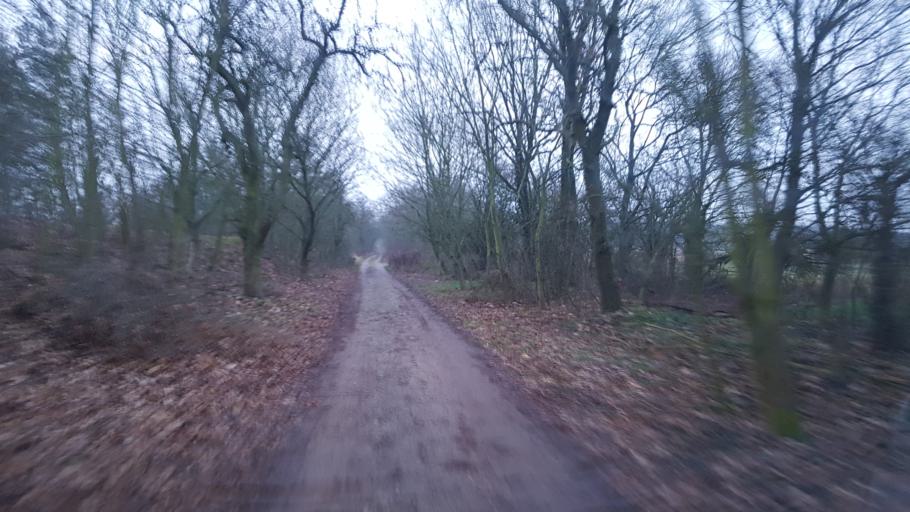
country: DE
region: Brandenburg
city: Stahnsdorf
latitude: 52.3622
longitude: 13.2006
